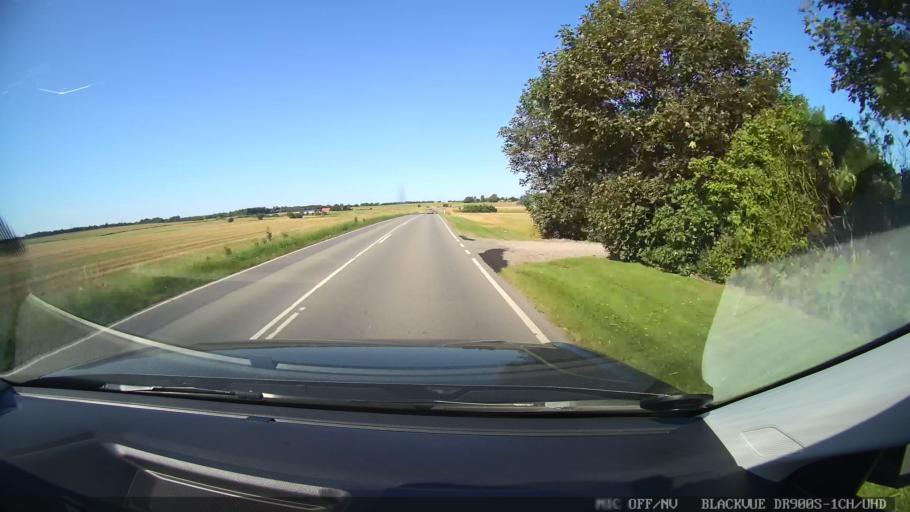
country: DK
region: Central Jutland
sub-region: Randers Kommune
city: Spentrup
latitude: 56.5337
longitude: 9.9992
